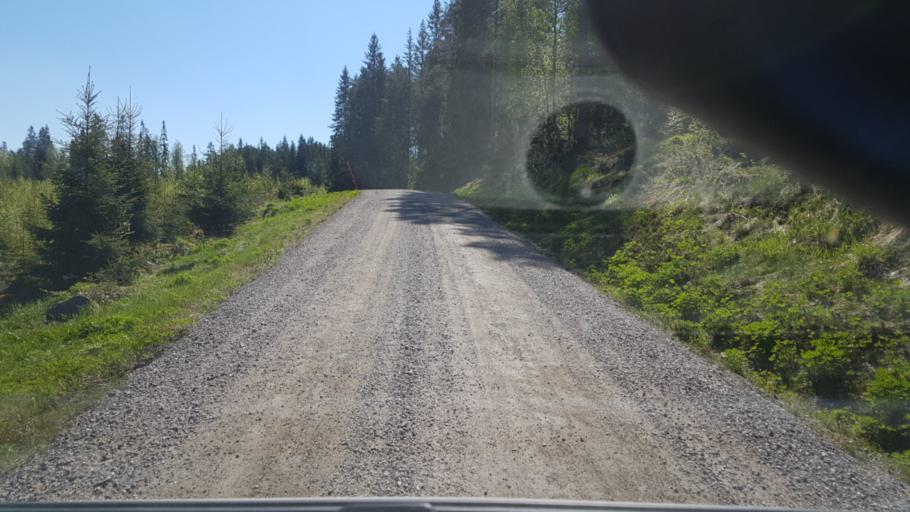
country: SE
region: Vaermland
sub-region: Eda Kommun
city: Charlottenberg
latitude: 60.0642
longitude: 12.5332
